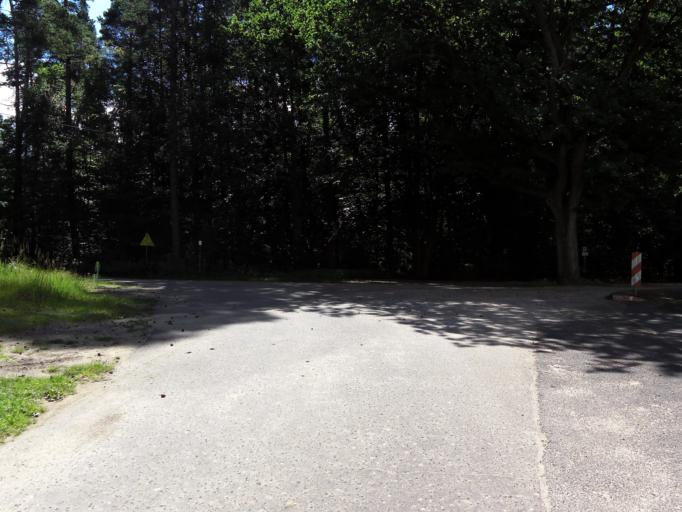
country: DE
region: Brandenburg
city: Lychen
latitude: 53.2153
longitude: 13.2799
